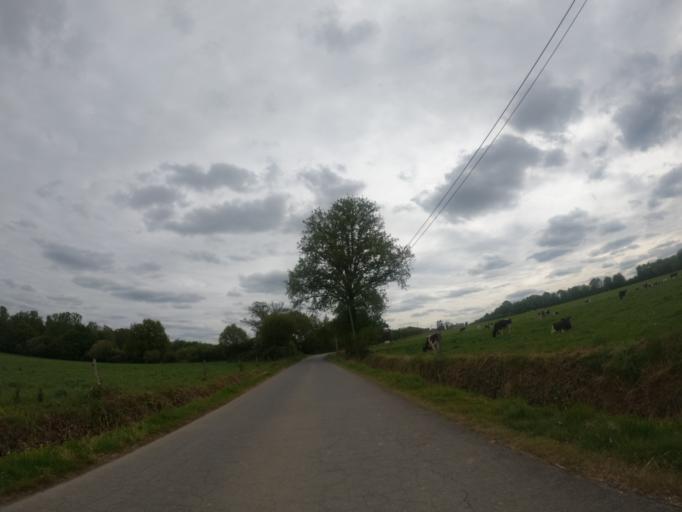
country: FR
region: Pays de la Loire
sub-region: Departement de la Loire-Atlantique
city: Rouge
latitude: 47.7359
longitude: -1.4308
